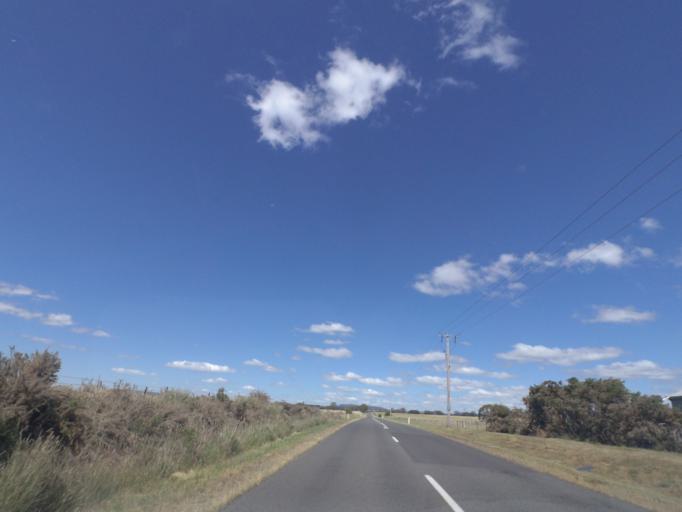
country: AU
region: Victoria
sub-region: Mount Alexander
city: Castlemaine
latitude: -37.2898
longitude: 144.4764
